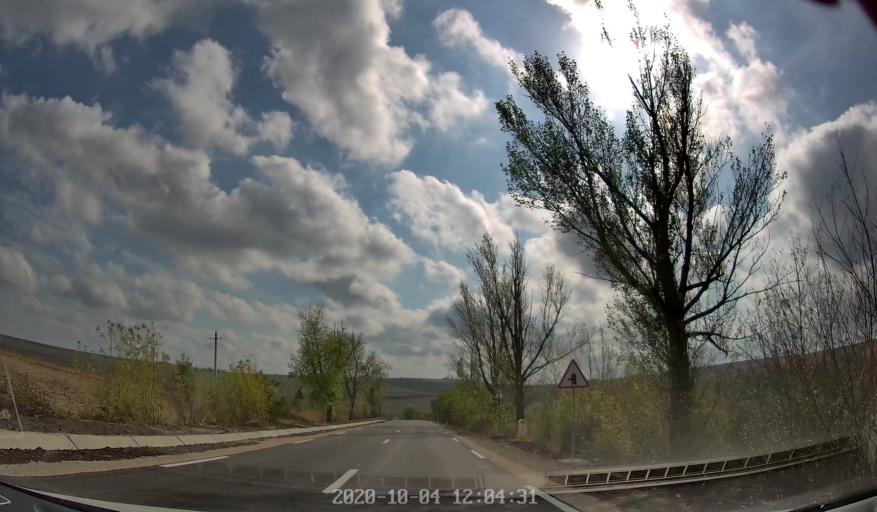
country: MD
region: Rezina
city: Saharna
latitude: 47.6030
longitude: 28.9439
